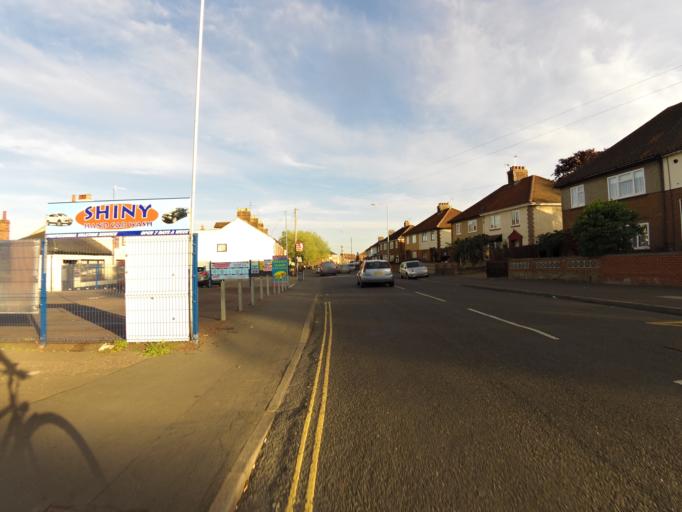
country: GB
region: England
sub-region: Norfolk
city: Norwich
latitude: 52.6441
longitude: 1.2917
